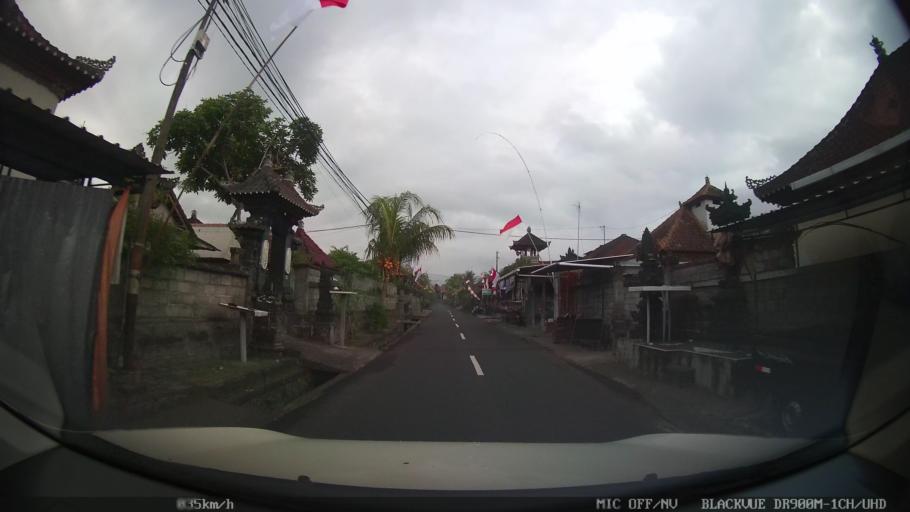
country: ID
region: Bali
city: Banjar Pasekan
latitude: -8.6198
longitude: 115.2980
